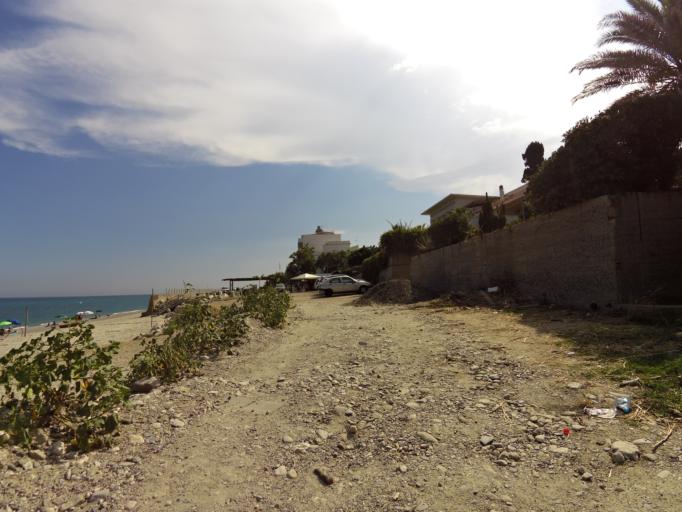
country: IT
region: Calabria
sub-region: Provincia di Reggio Calabria
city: Monasterace Marina
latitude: 38.4435
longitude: 16.5785
